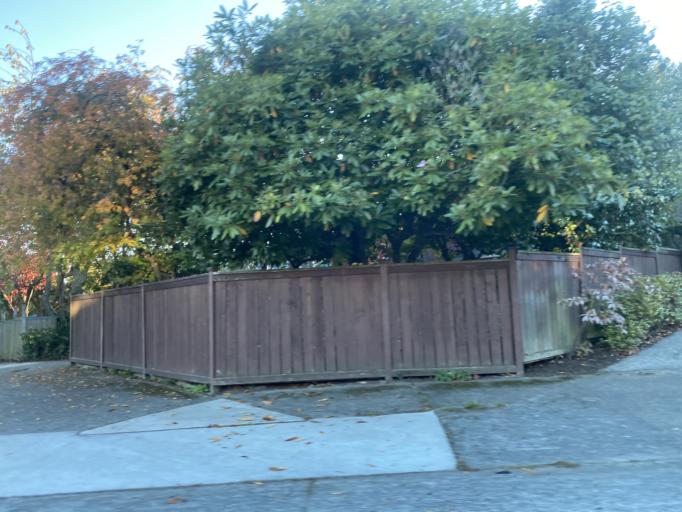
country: US
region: Washington
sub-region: King County
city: Seattle
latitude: 47.6373
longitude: -122.4031
